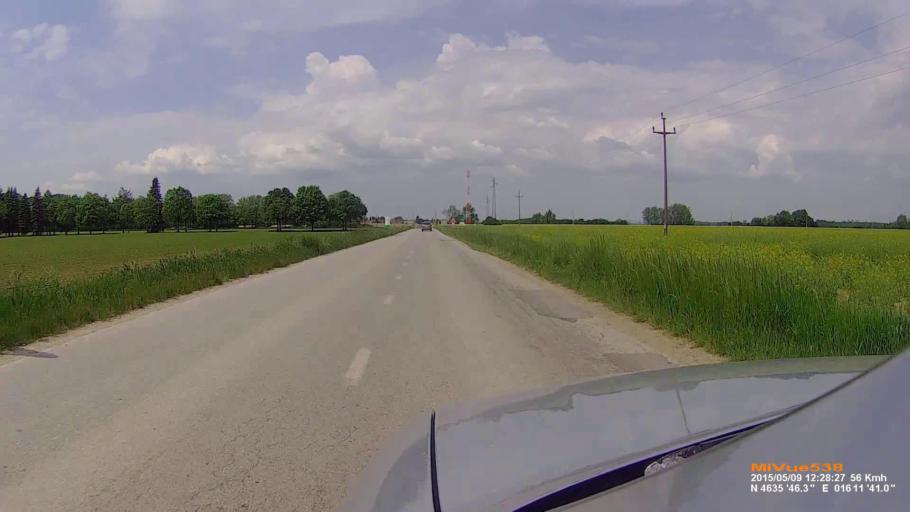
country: SI
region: Verzej
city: Verzej
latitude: 46.5963
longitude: 16.1947
